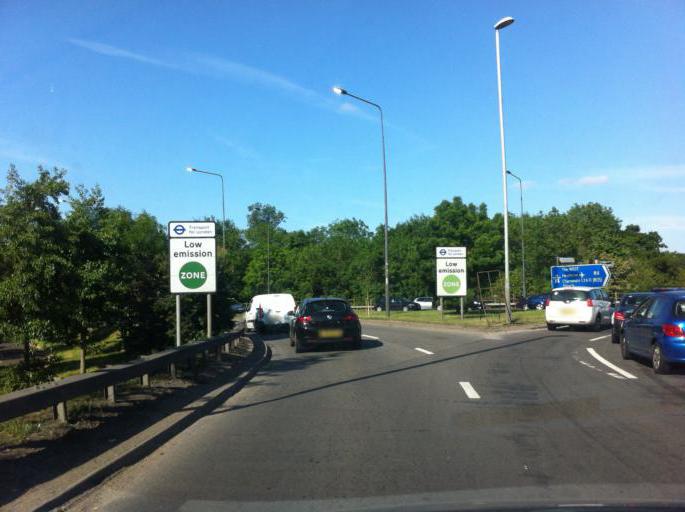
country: GB
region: England
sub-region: Greater London
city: Hayes
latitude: 51.4917
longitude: -0.4096
